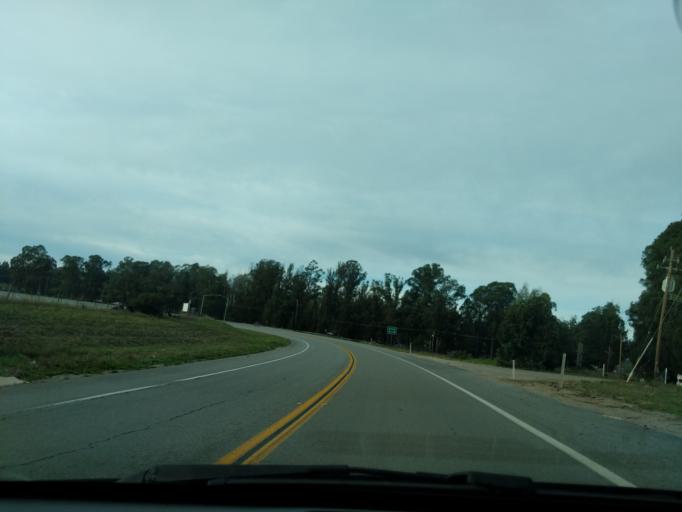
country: US
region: California
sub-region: San Luis Obispo County
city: Callender
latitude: 35.0450
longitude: -120.5683
